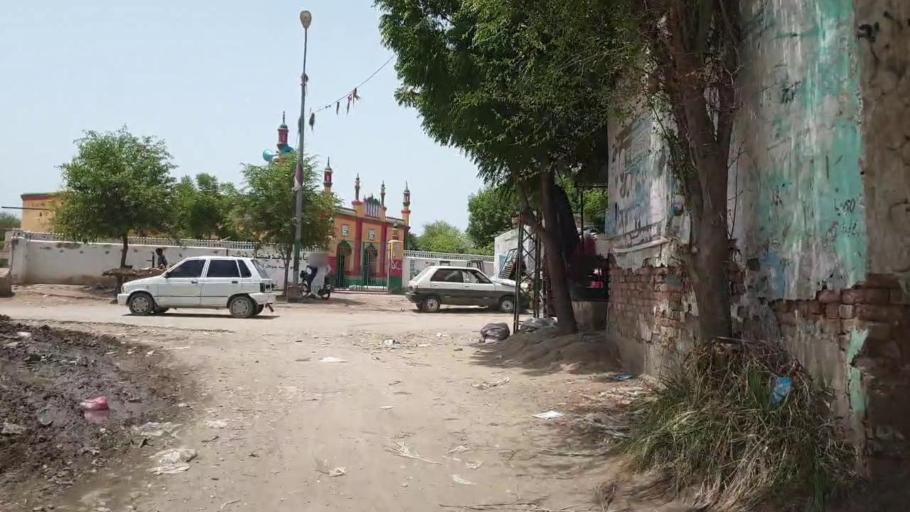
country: PK
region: Sindh
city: Daur
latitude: 26.4000
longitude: 68.4381
